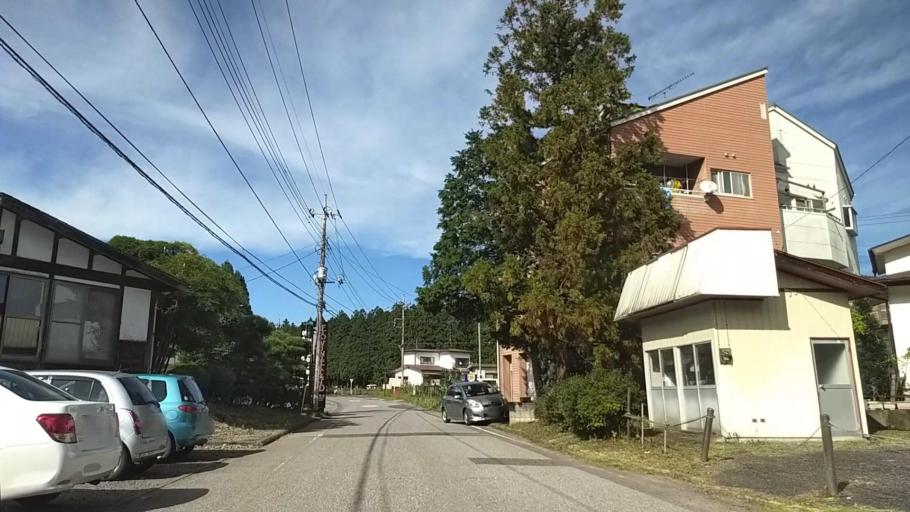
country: JP
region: Tochigi
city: Imaichi
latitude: 36.7902
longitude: 139.6978
